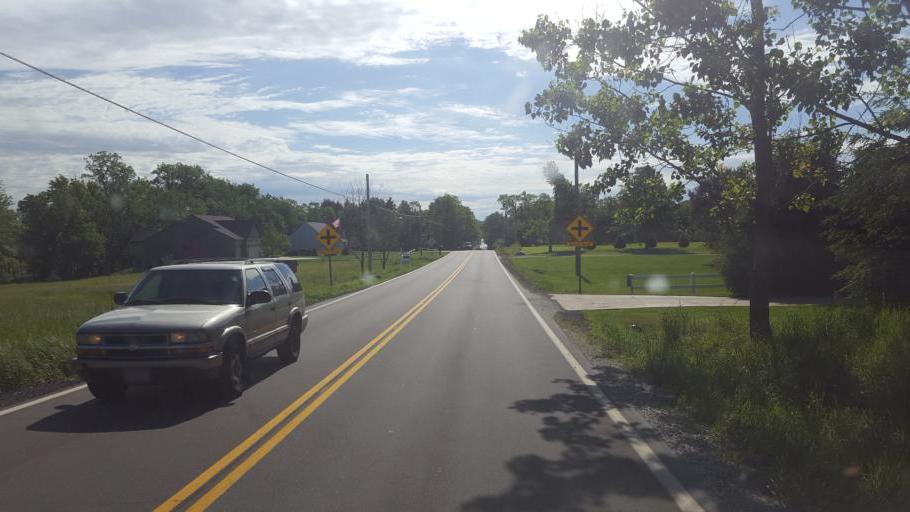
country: US
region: Ohio
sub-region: Medina County
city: Wadsworth
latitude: 41.0993
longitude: -81.7592
